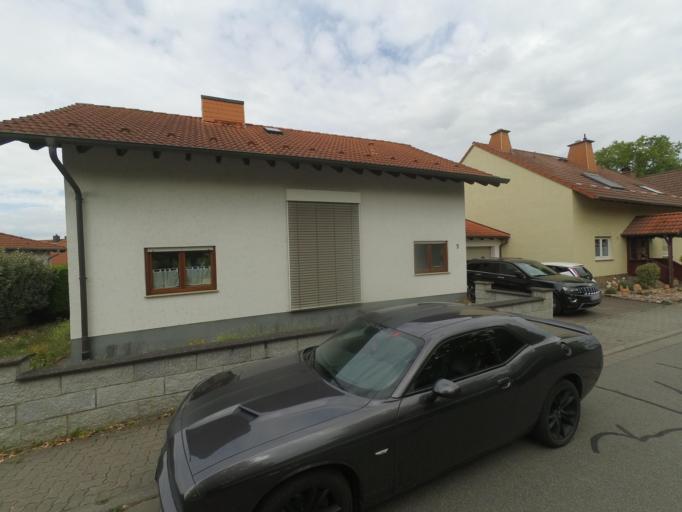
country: DE
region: Hesse
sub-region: Regierungsbezirk Darmstadt
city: Einhausen
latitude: 49.6951
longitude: 8.5716
